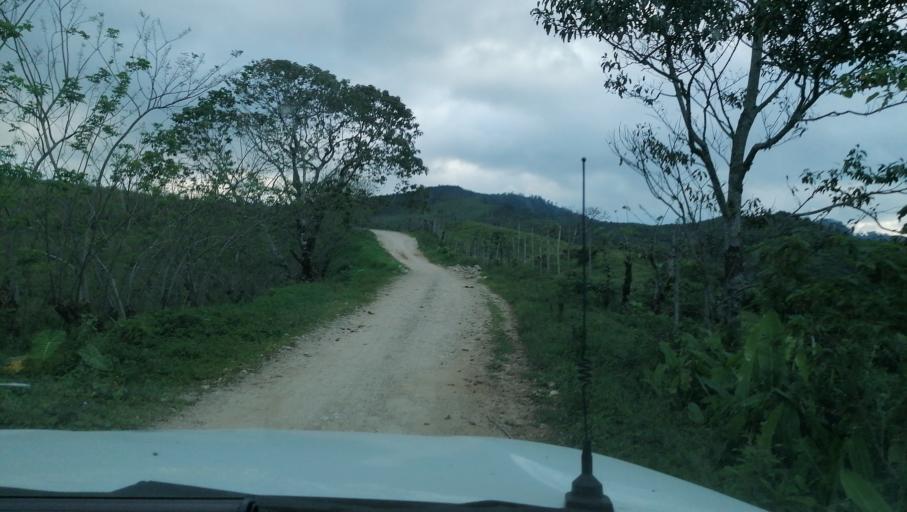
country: MX
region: Chiapas
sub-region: Francisco Leon
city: San Miguel la Sardina
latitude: 17.2912
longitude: -93.2699
